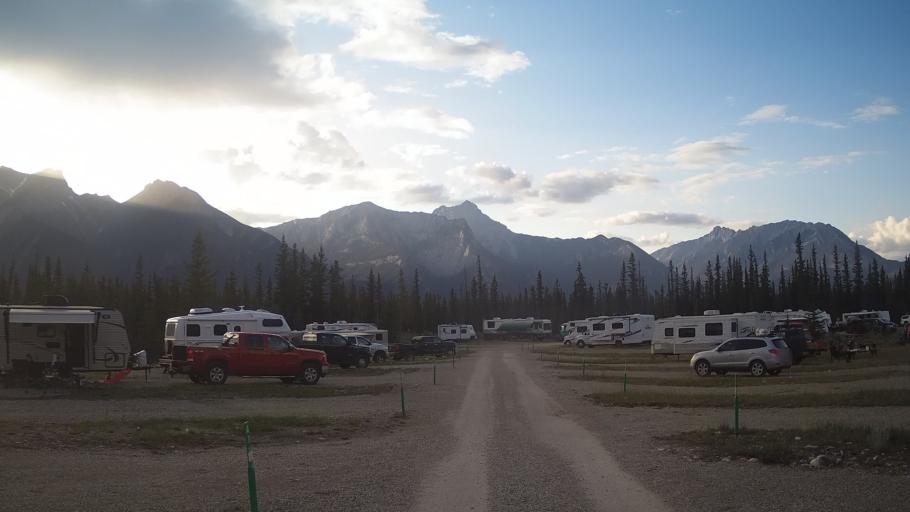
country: CA
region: Alberta
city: Jasper Park Lodge
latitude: 53.0172
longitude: -118.0865
